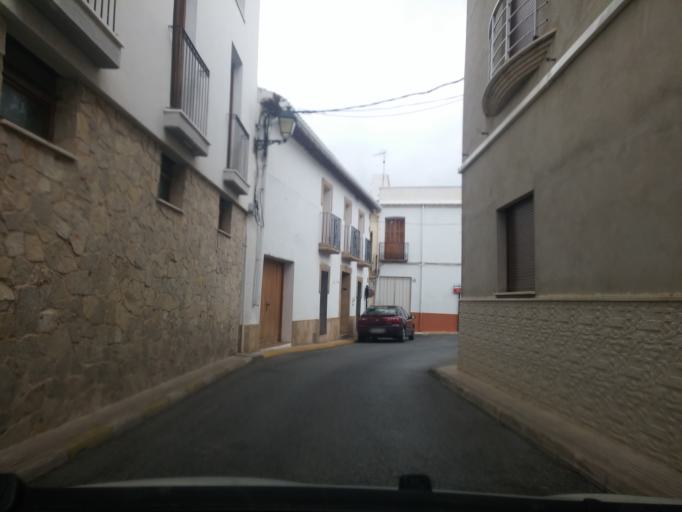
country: ES
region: Valencia
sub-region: Provincia de Alicante
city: Jalon
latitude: 38.7429
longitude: 0.0058
